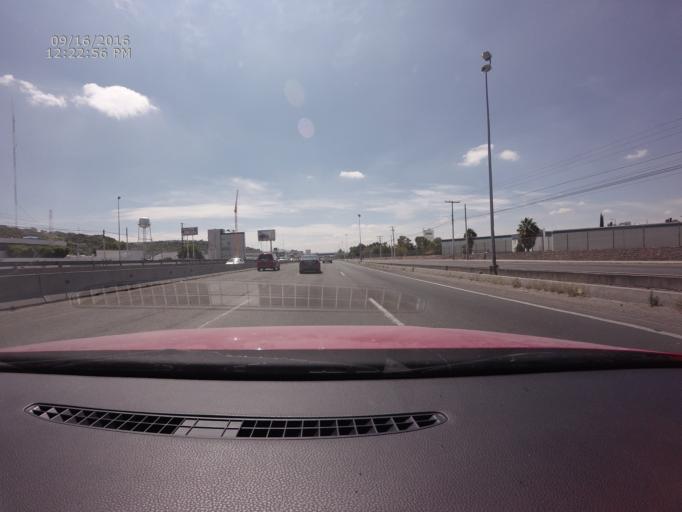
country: MX
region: Queretaro
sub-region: Queretaro
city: Sergio Villasenor
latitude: 20.6331
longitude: -100.4272
